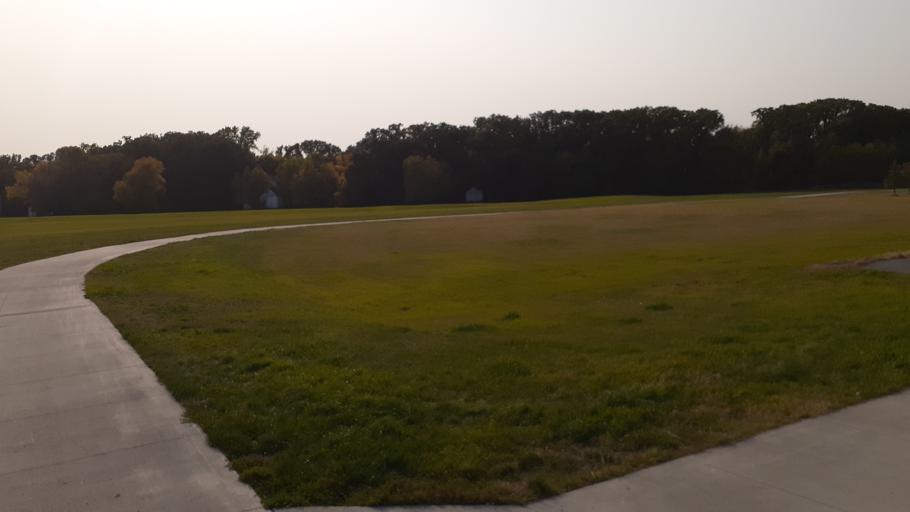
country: US
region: Minnesota
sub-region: Clay County
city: Oakport
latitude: 46.9103
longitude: -96.7554
